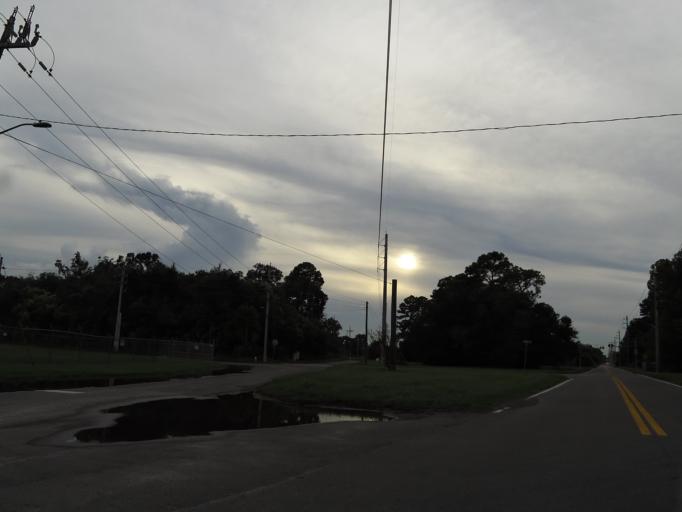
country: US
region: Florida
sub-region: Duval County
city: Jacksonville
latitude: 30.3563
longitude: -81.7156
